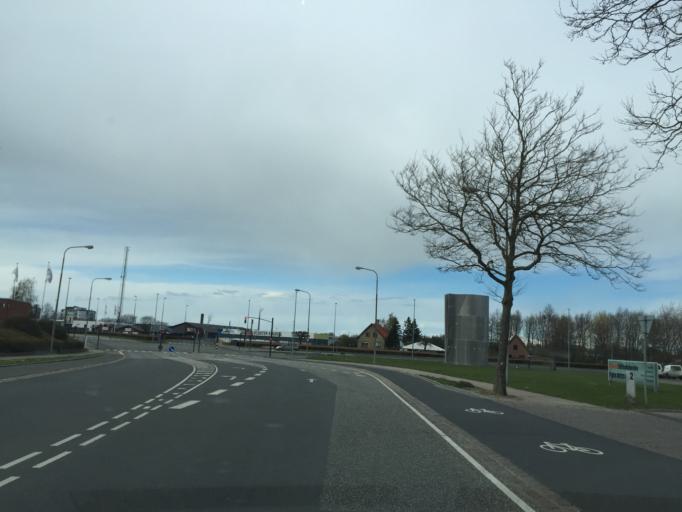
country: DK
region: South Denmark
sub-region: Odense Kommune
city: Neder Holluf
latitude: 55.3903
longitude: 10.4389
